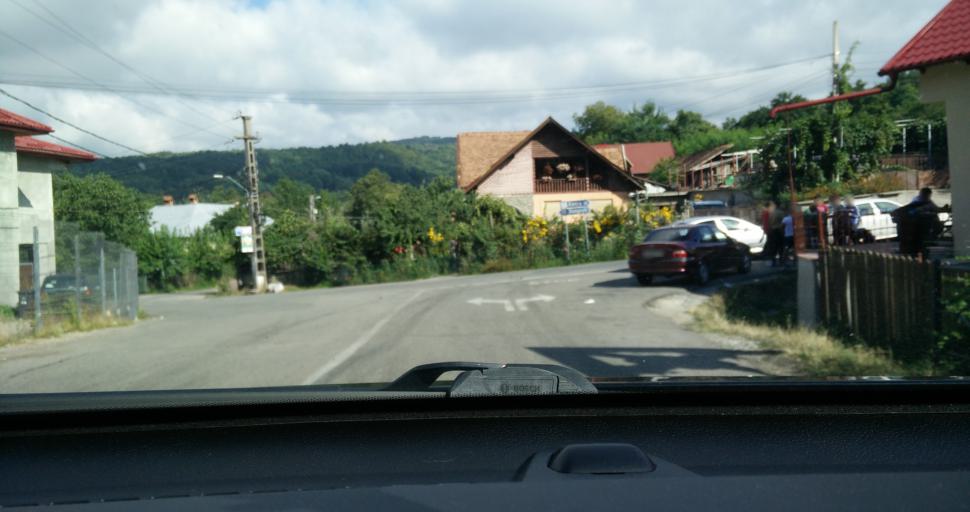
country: RO
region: Gorj
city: Novaci-Straini
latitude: 45.1772
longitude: 23.6719
